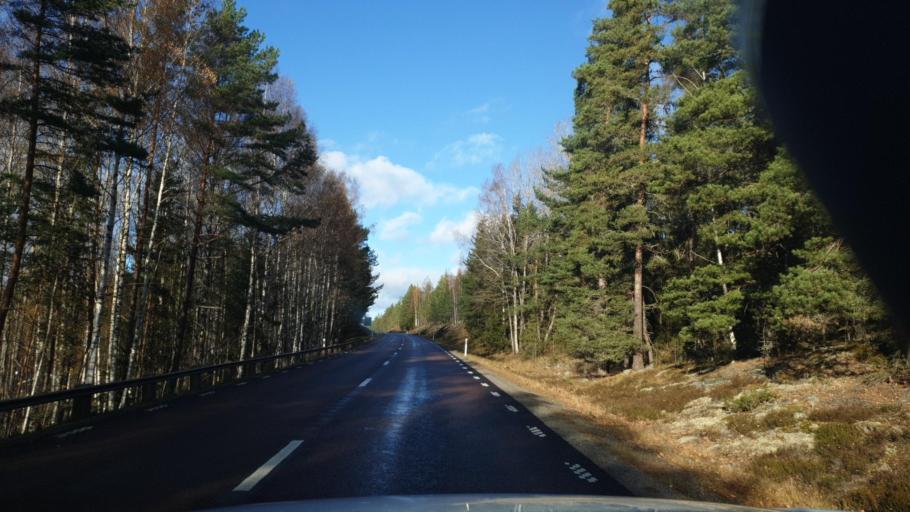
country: SE
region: Vaermland
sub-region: Arvika Kommun
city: Arvika
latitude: 59.5638
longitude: 12.7216
